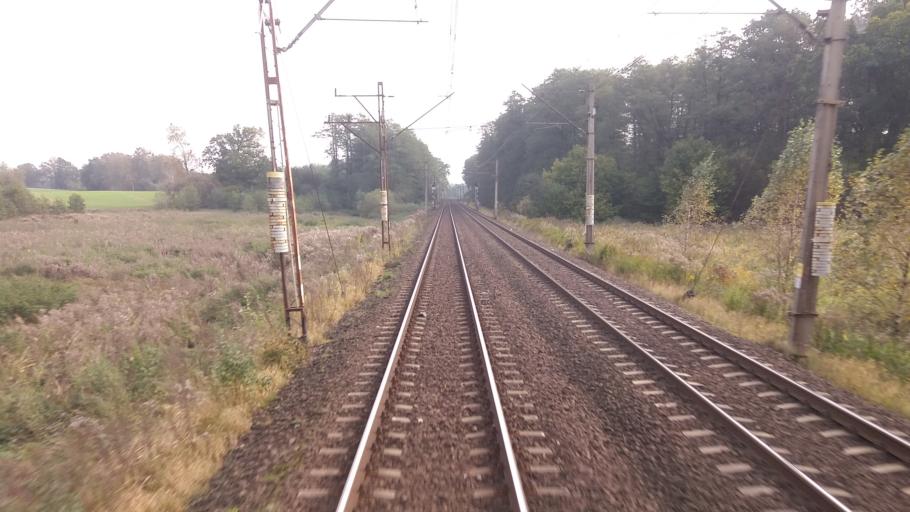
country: PL
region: West Pomeranian Voivodeship
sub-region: Powiat stargardzki
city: Dolice
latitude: 53.1842
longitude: 15.2643
